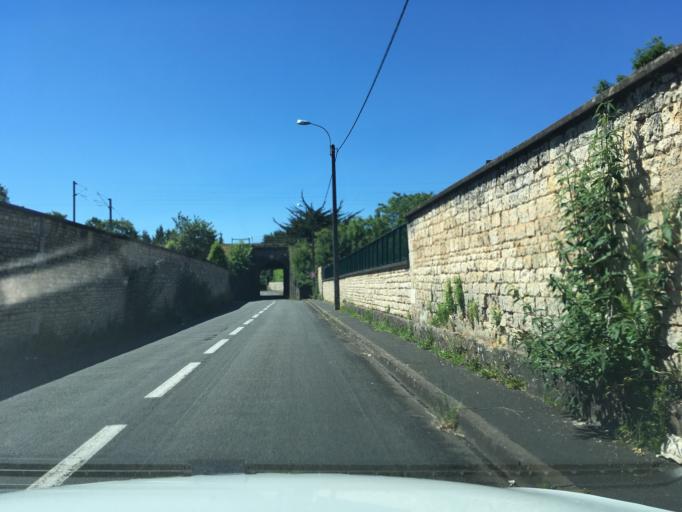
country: FR
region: Poitou-Charentes
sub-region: Departement des Deux-Sevres
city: Niort
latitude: 46.3239
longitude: -0.4431
